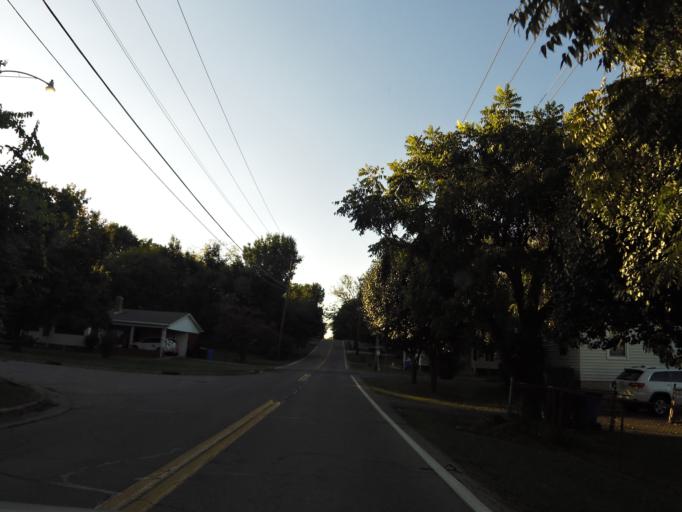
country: US
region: Tennessee
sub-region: Blount County
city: Alcoa
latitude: 35.7765
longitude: -83.9601
